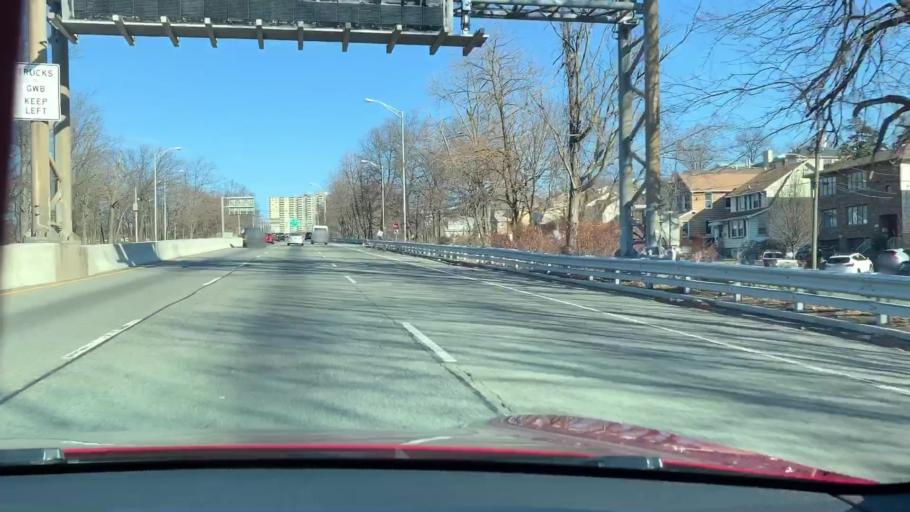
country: US
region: New Jersey
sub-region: Bergen County
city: Palisades Park
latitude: 40.8474
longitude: -73.9895
